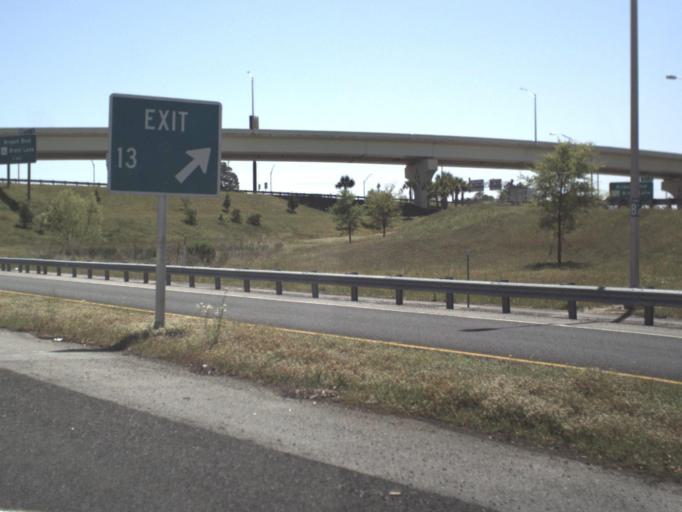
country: US
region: Florida
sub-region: Escambia County
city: Ferry Pass
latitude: 30.5033
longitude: -87.2316
